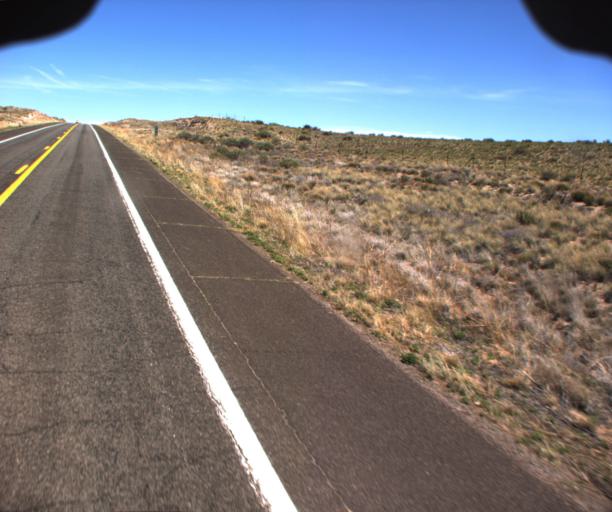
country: US
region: Arizona
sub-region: Mohave County
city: Peach Springs
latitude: 35.5158
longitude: -113.4994
